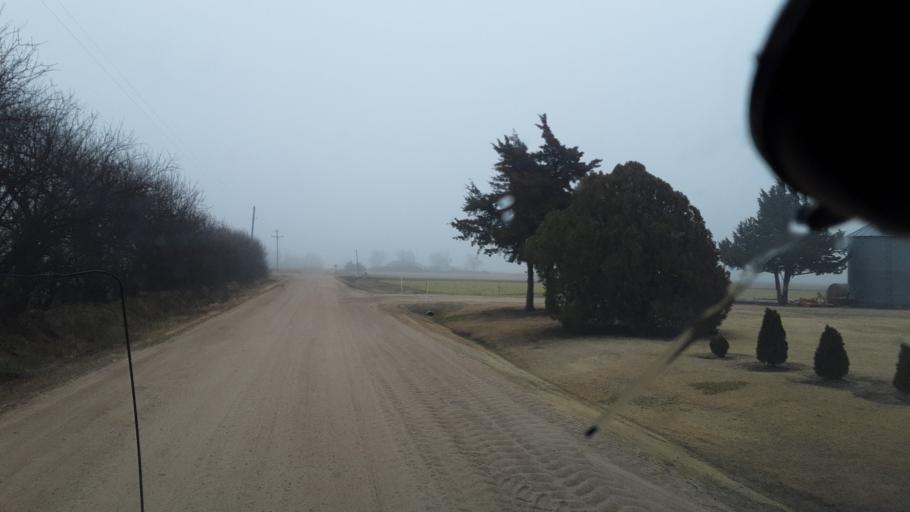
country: US
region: Kansas
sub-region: Reno County
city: South Hutchinson
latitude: 37.9845
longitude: -97.9974
